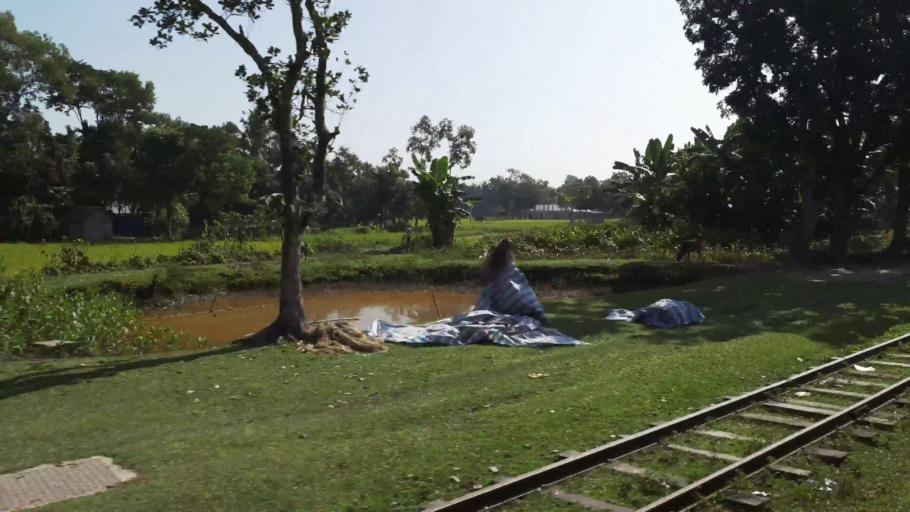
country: BD
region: Dhaka
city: Gafargaon
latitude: 24.5872
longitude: 90.5065
